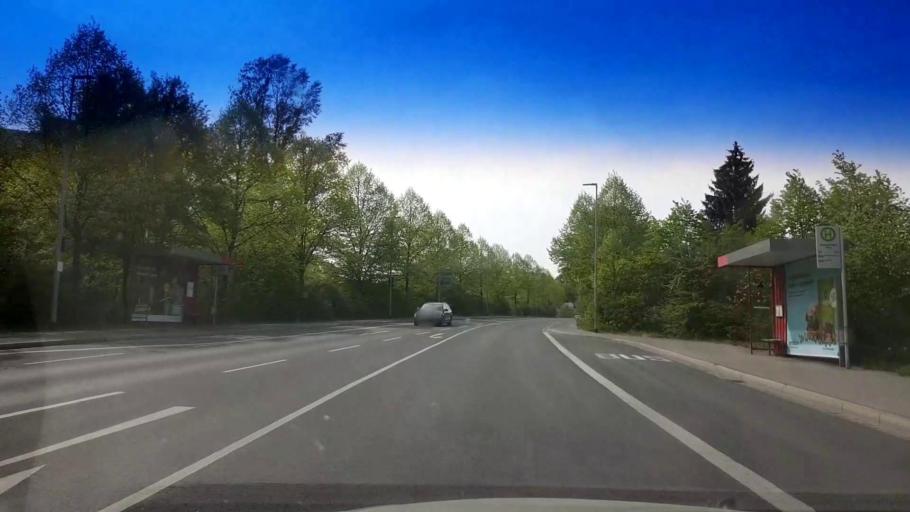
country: DE
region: Bavaria
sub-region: Upper Franconia
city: Bamberg
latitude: 49.9005
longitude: 10.8755
